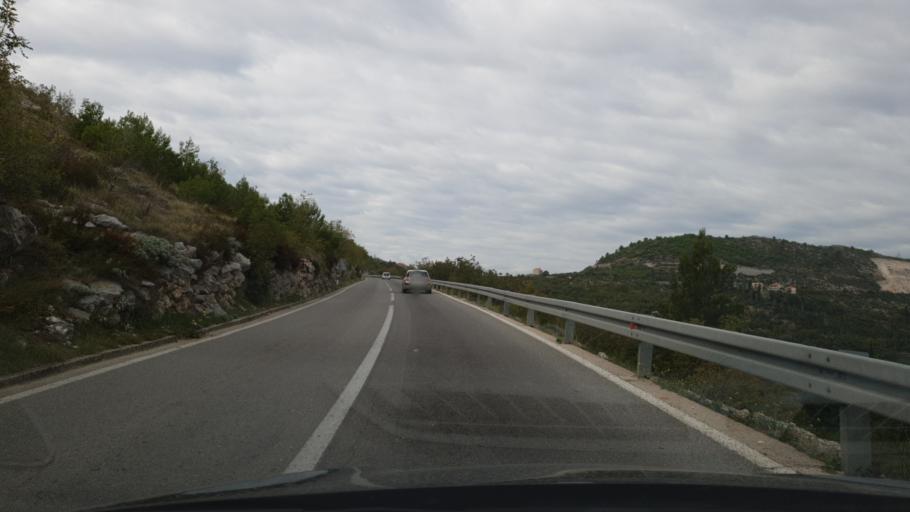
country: HR
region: Dubrovacko-Neretvanska
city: Cibaca
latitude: 42.6415
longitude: 18.1665
